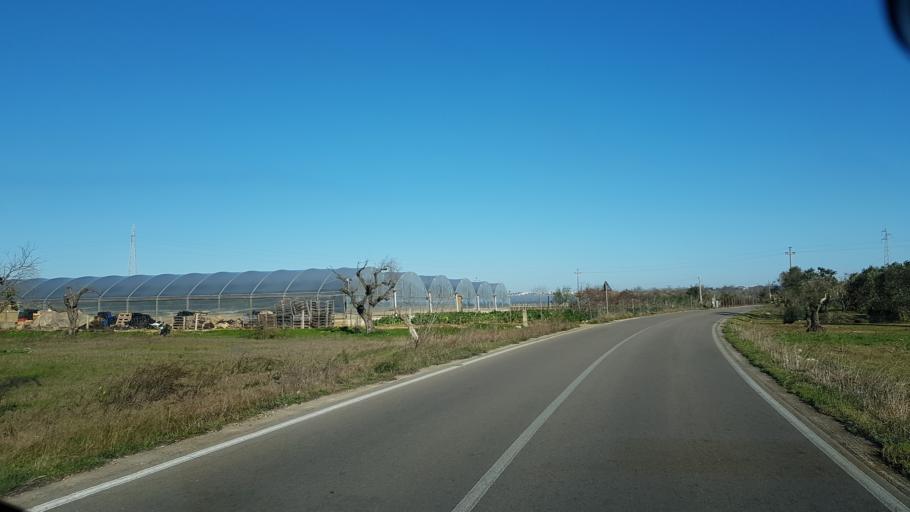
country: IT
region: Apulia
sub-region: Provincia di Lecce
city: Melissano
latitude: 39.9934
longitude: 18.1112
